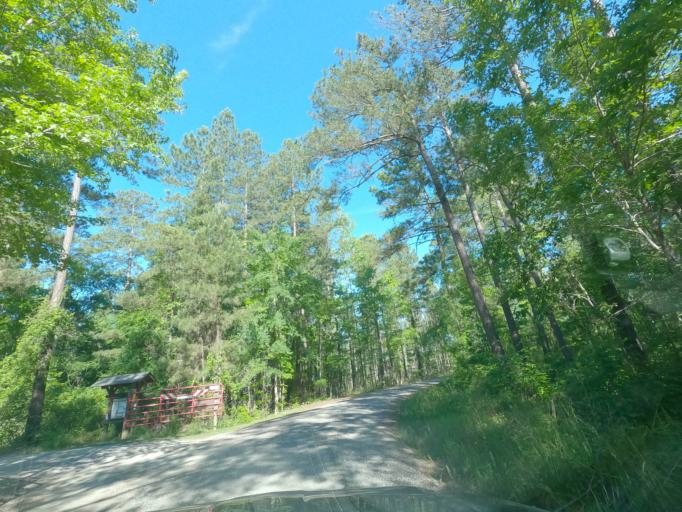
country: US
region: Georgia
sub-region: Columbia County
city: Evans
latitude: 33.6142
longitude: -82.1137
